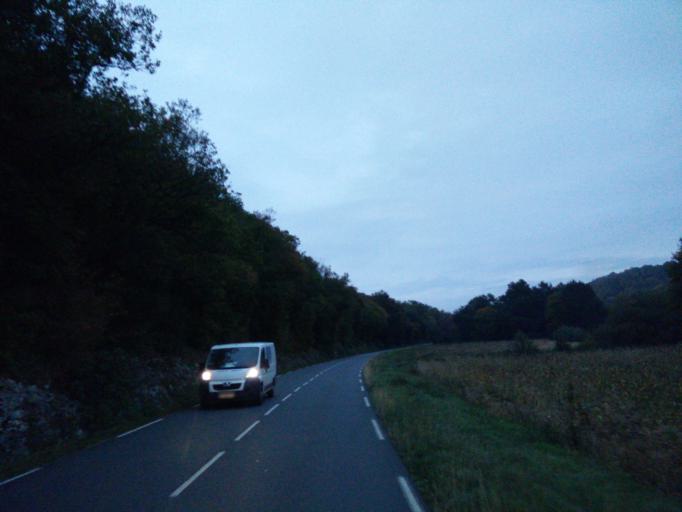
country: FR
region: Aquitaine
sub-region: Departement de la Dordogne
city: Saint-Cyprien
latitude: 44.9218
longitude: 1.0951
